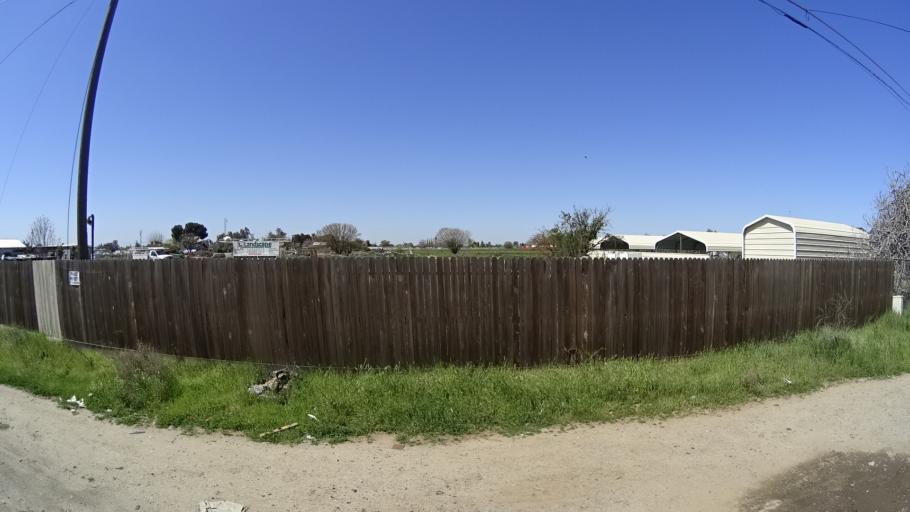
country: US
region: California
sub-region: Fresno County
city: West Park
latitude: 36.7550
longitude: -119.8444
